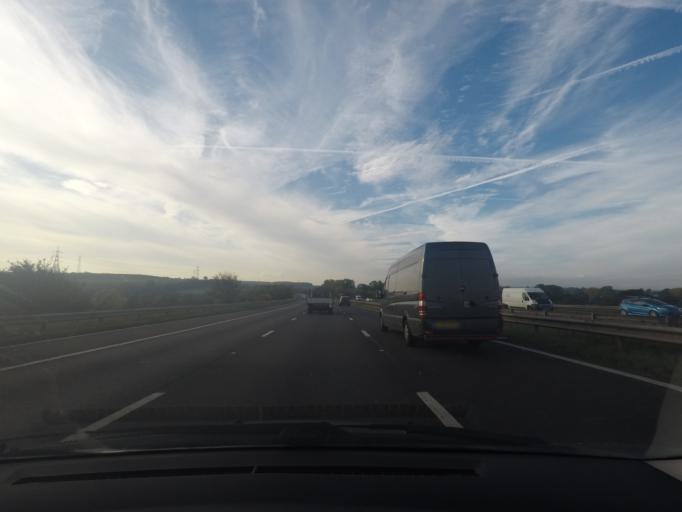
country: GB
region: England
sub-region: Barnsley
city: Darton
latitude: 53.5773
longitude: -1.5393
